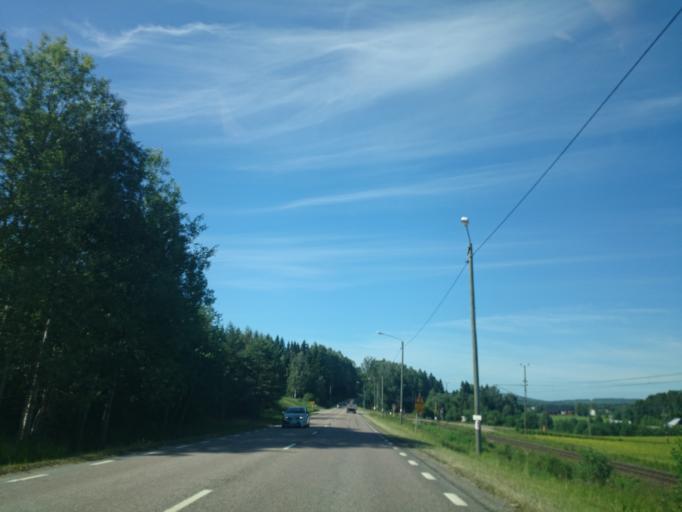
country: SE
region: Vaesternorrland
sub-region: Sundsvalls Kommun
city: Vi
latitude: 62.3956
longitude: 17.1974
